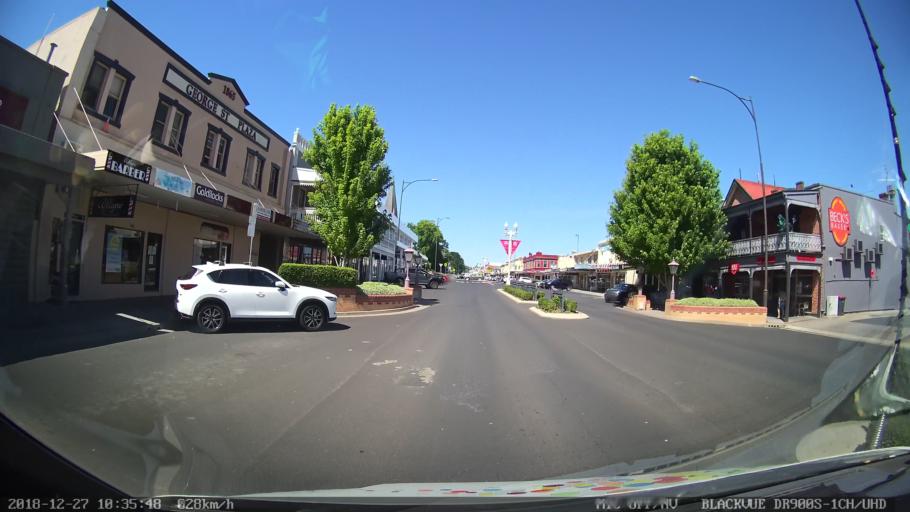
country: AU
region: New South Wales
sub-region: Bathurst Regional
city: Bathurst
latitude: -33.4151
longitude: 149.5809
